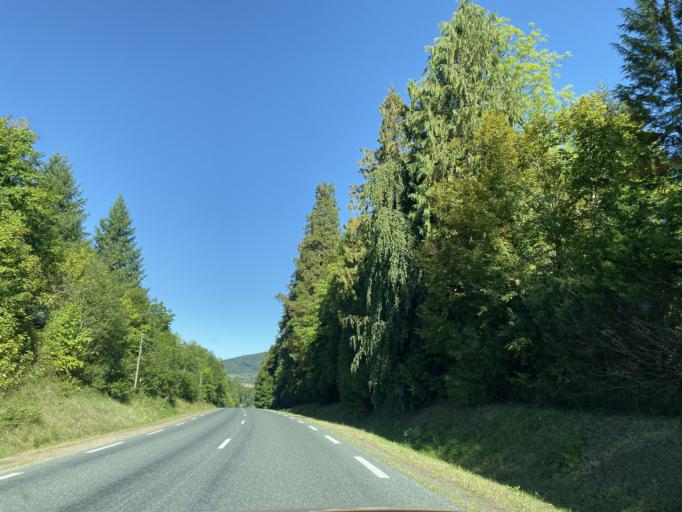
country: FR
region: Rhone-Alpes
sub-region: Departement de la Loire
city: Saint-Just-en-Chevalet
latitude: 45.8978
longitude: 3.8476
